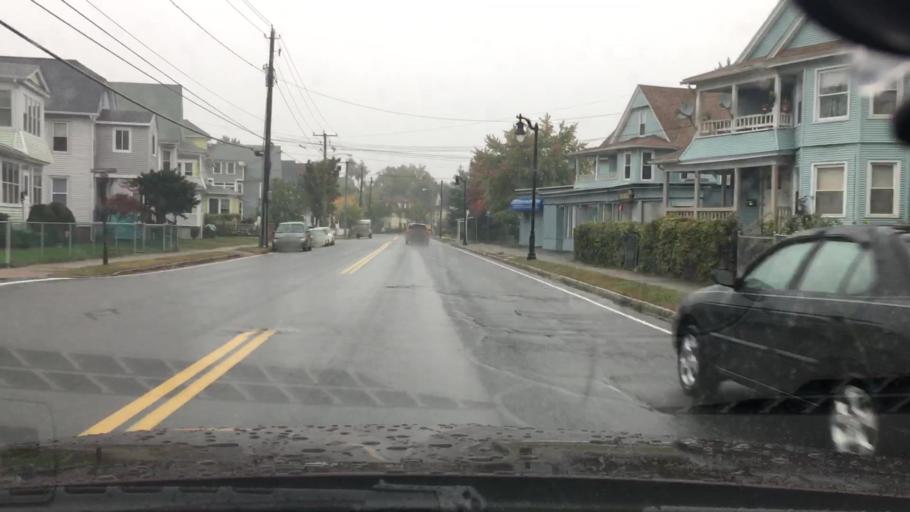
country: US
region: Massachusetts
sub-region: Hampden County
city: Springfield
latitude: 42.0813
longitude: -72.5546
